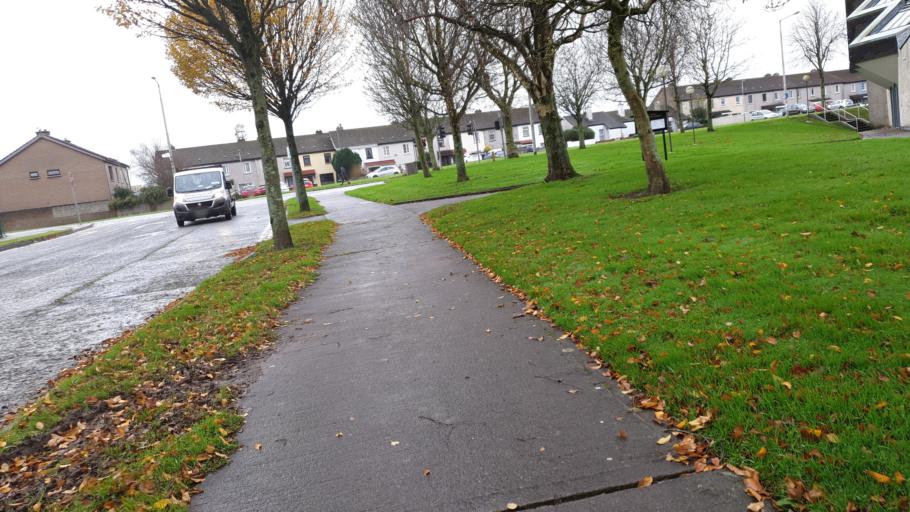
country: IE
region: Munster
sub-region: County Cork
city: Passage West
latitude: 51.8913
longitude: -8.4043
